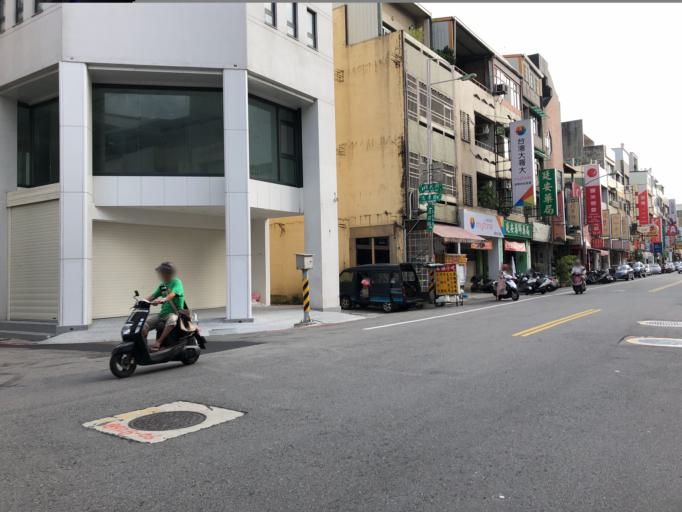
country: TW
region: Taiwan
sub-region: Miaoli
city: Miaoli
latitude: 24.5610
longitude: 120.8188
